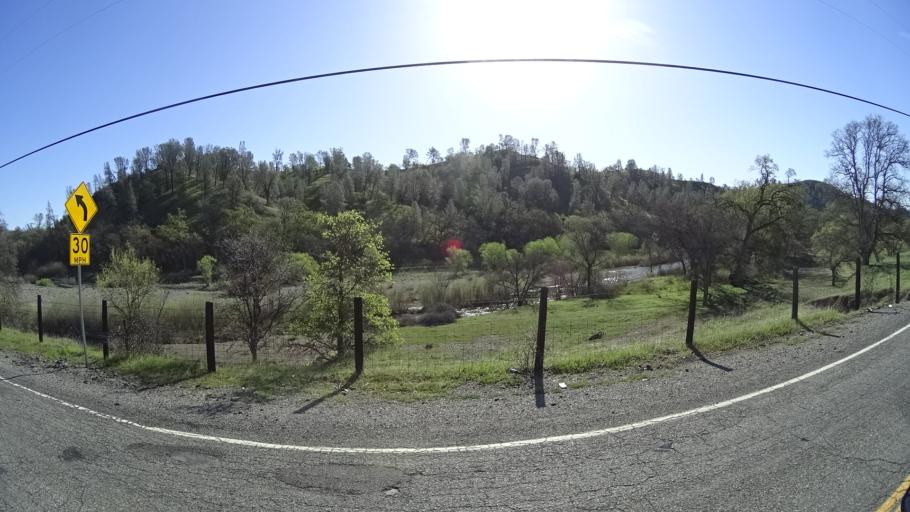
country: US
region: California
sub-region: Glenn County
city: Orland
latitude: 39.6671
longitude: -122.5256
